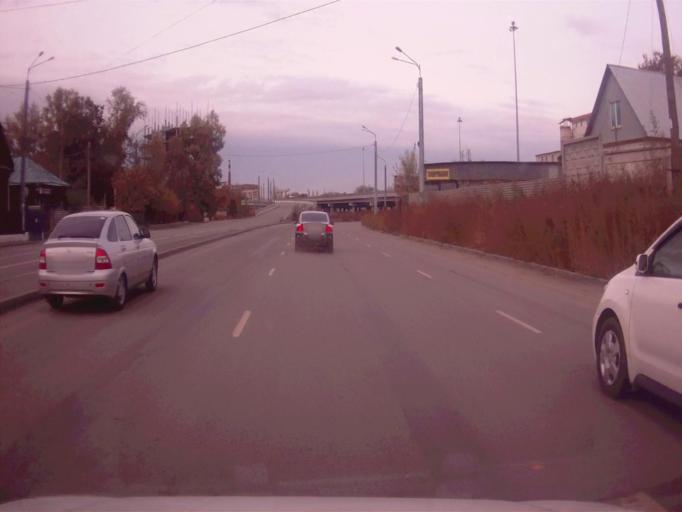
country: RU
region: Chelyabinsk
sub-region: Gorod Chelyabinsk
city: Chelyabinsk
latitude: 55.1683
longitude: 61.4111
